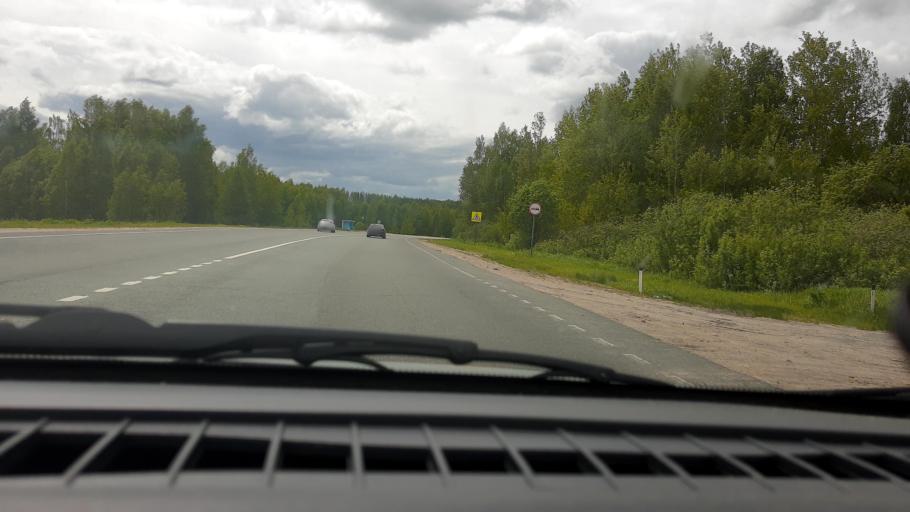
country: RU
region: Nizjnij Novgorod
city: Vladimirskoye
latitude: 56.9143
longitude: 45.0514
